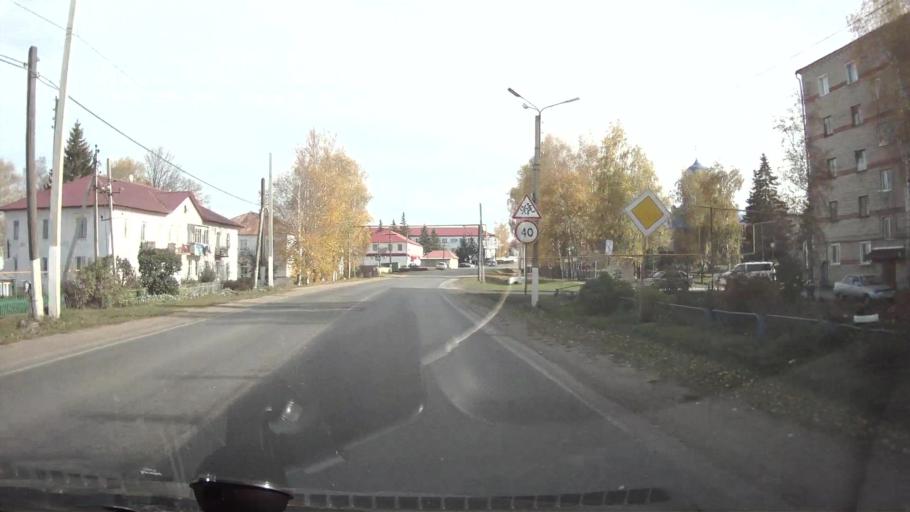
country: RU
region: Mordoviya
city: Turgenevo
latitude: 54.8464
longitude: 46.3346
